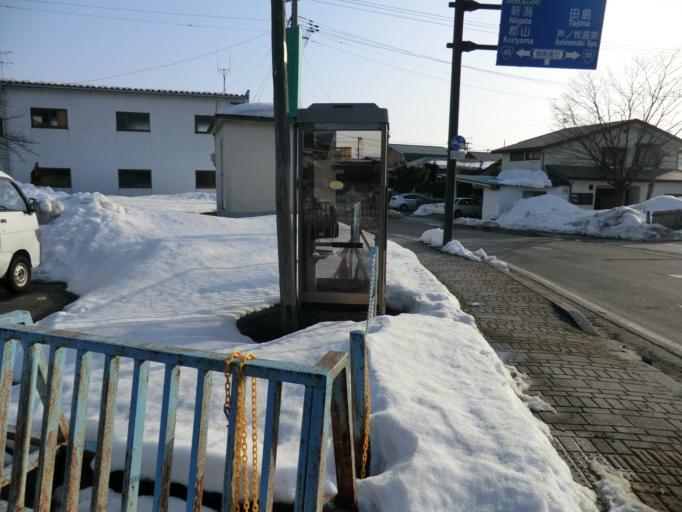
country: JP
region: Fukushima
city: Kitakata
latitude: 37.4852
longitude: 139.9356
